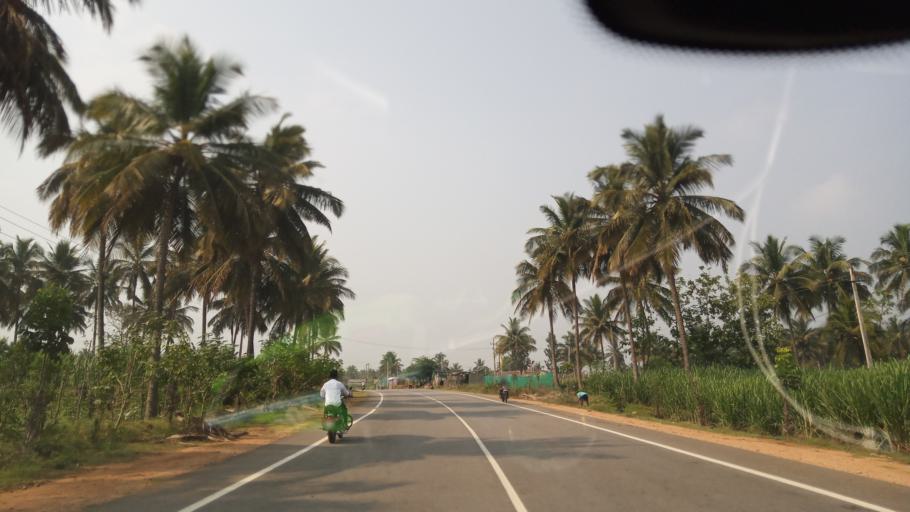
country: IN
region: Karnataka
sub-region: Mandya
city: Pandavapura
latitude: 12.5406
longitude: 76.6702
